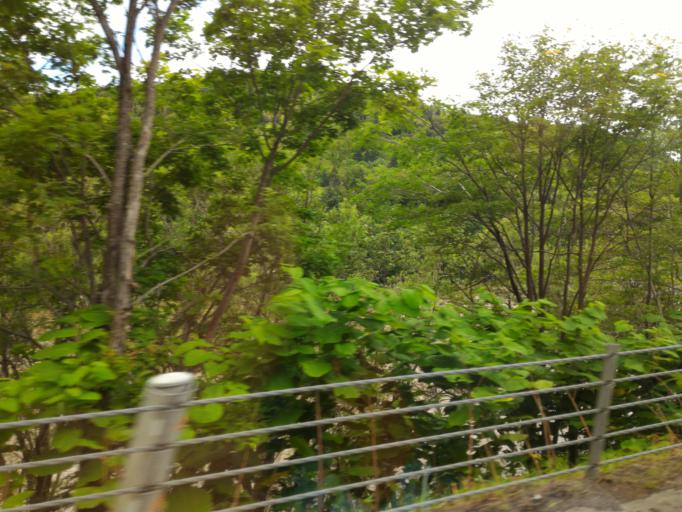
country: JP
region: Hokkaido
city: Nayoro
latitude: 44.7249
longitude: 142.2355
